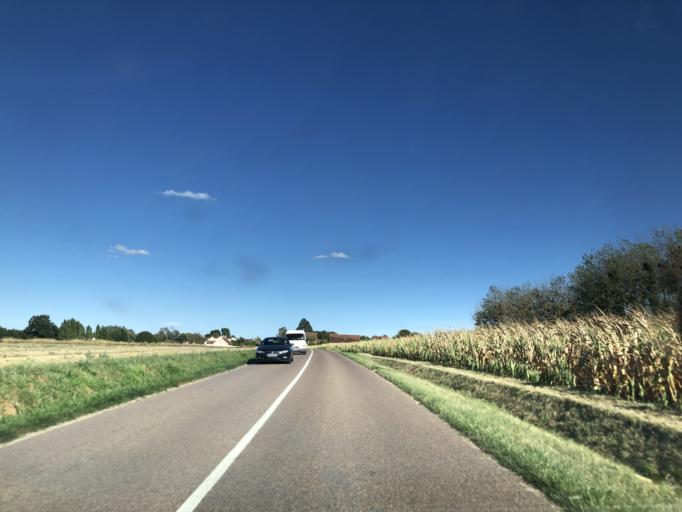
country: FR
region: Bourgogne
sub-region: Departement de l'Yonne
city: Hery
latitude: 47.9017
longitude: 3.6155
